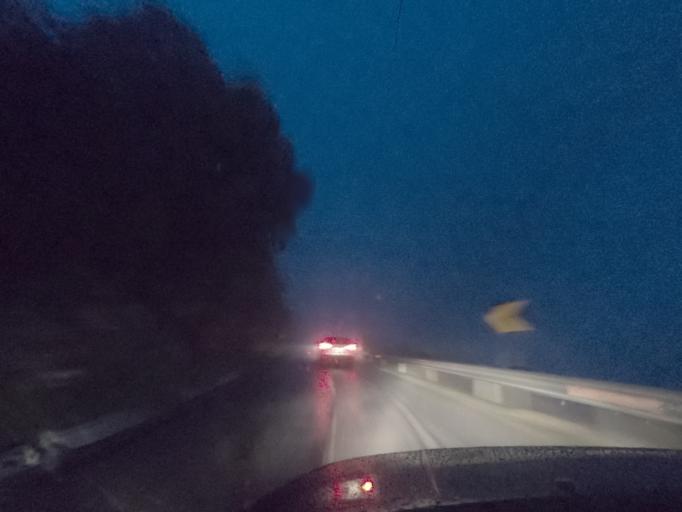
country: PT
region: Vila Real
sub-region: Sabrosa
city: Vilela
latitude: 41.2158
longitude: -7.5525
